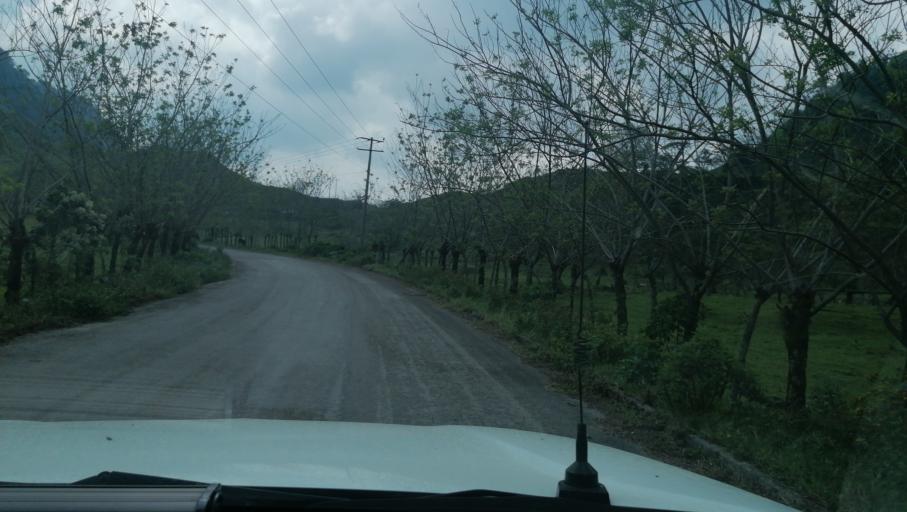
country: MX
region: Chiapas
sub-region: Francisco Leon
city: San Miguel la Sardina
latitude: 17.2517
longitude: -93.2787
